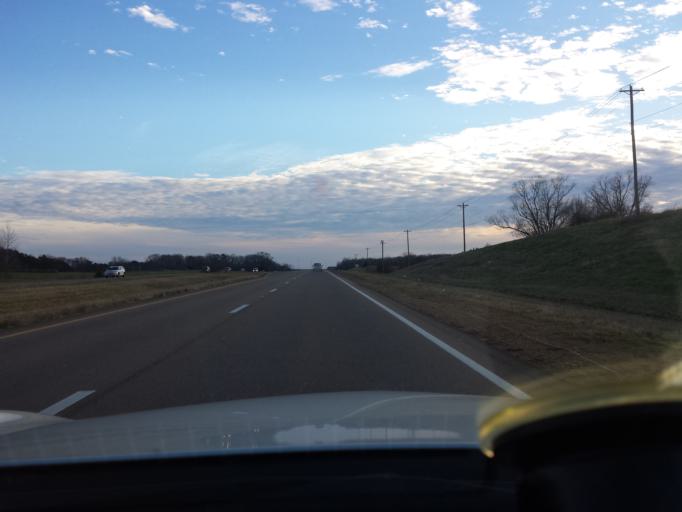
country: US
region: Mississippi
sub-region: Oktibbeha County
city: Starkville
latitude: 33.4797
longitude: -88.8515
